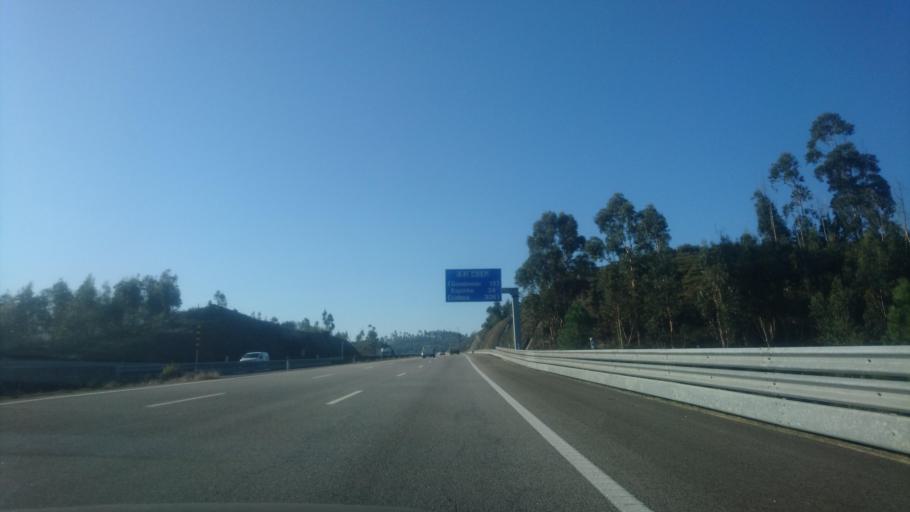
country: PT
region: Porto
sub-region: Paredes
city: Recarei
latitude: 41.1327
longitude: -8.4275
